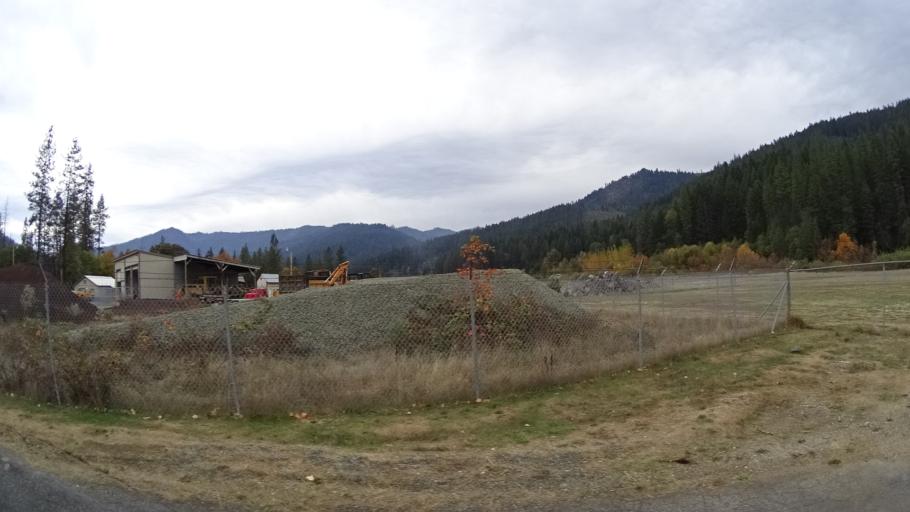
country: US
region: California
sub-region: Siskiyou County
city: Happy Camp
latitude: 41.7904
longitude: -123.3871
